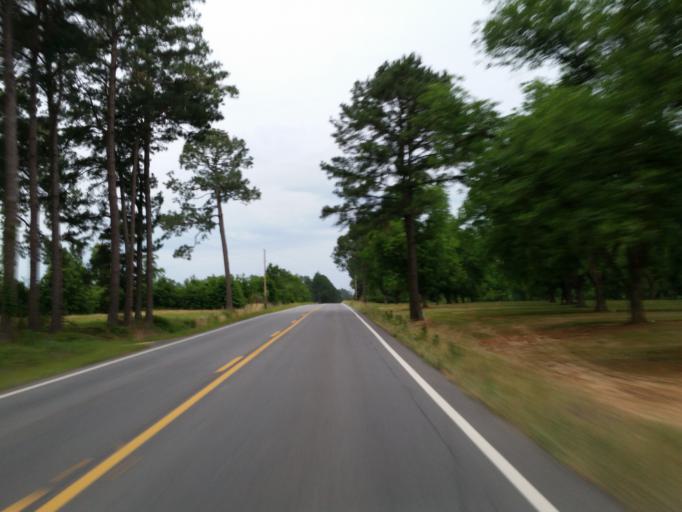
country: US
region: Georgia
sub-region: Crisp County
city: Cordele
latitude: 31.8926
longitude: -83.7584
